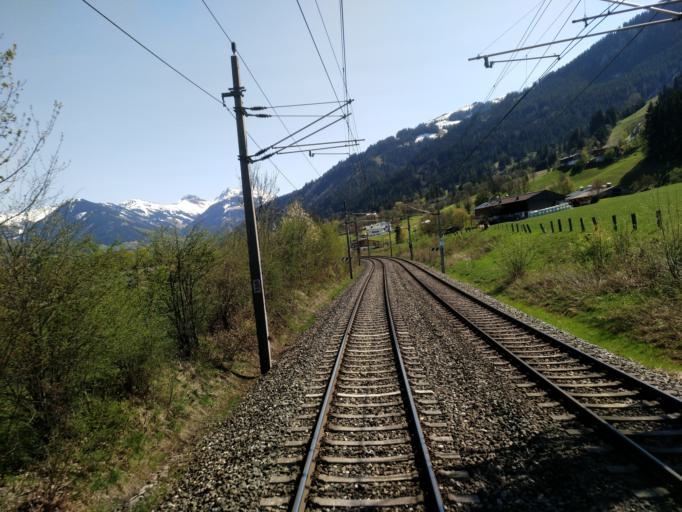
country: AT
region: Tyrol
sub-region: Politischer Bezirk Kitzbuhel
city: Kitzbuhel
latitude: 47.4486
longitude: 12.3823
